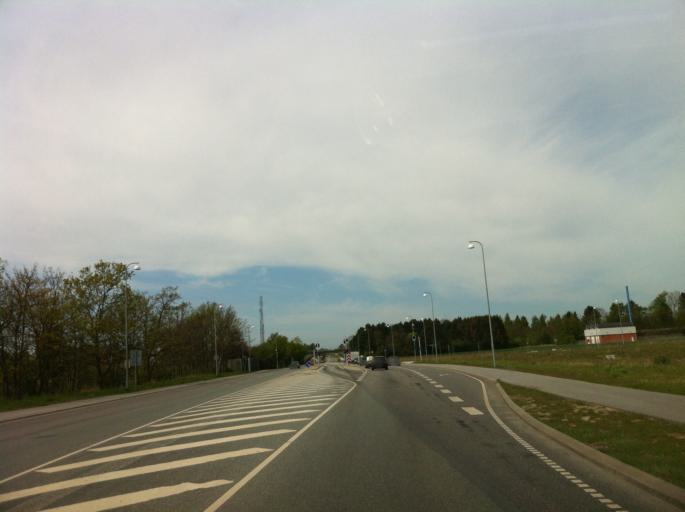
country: DK
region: Zealand
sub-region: Naestved Kommune
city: Naestved
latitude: 55.2439
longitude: 11.7744
